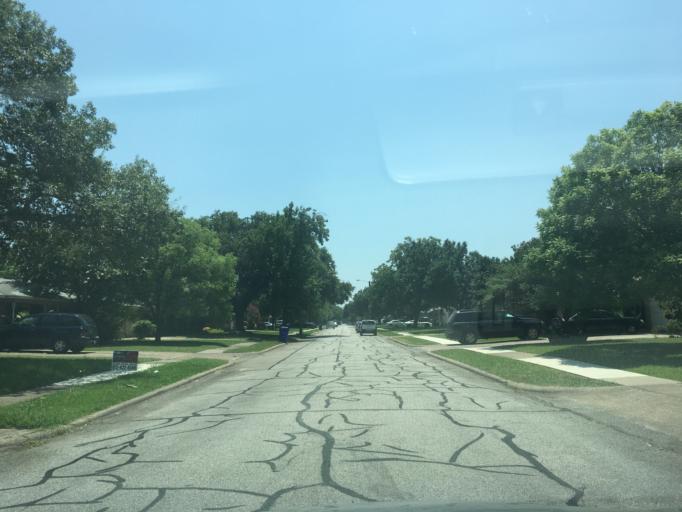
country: US
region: Texas
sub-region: Dallas County
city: Farmers Branch
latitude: 32.9346
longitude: -96.8794
